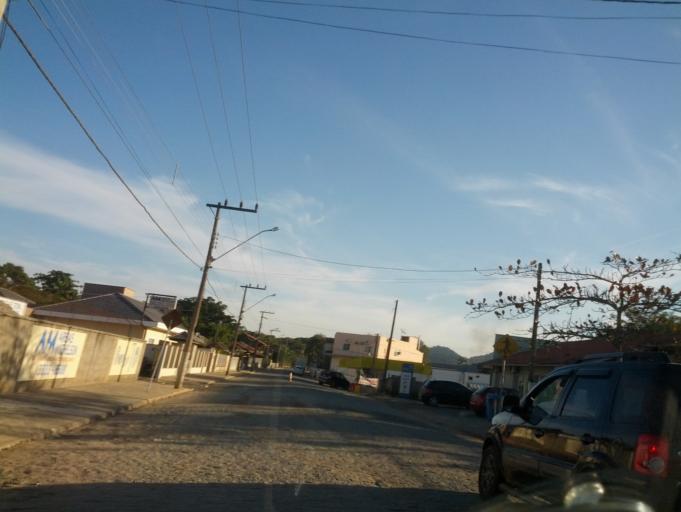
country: BR
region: Santa Catarina
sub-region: Indaial
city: Indaial
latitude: -26.9032
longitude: -49.2589
